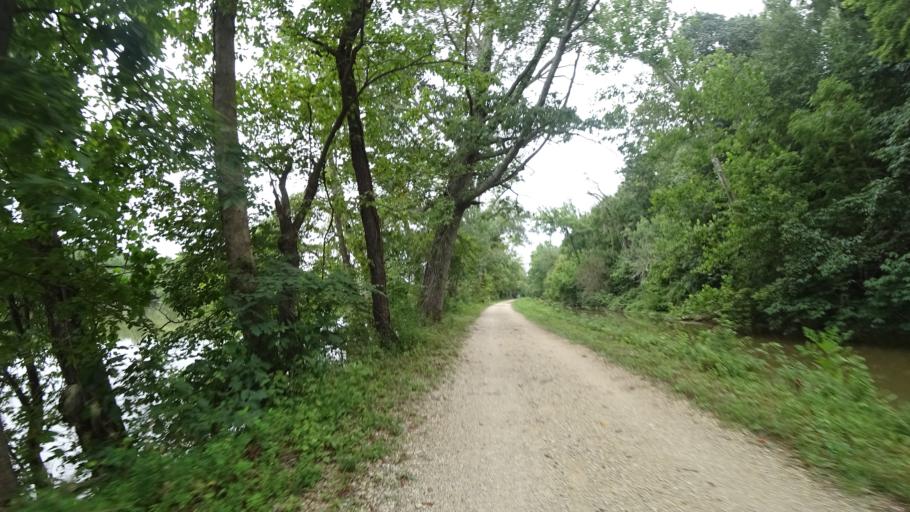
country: US
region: Maryland
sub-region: Montgomery County
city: Travilah
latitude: 39.0409
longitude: -77.2648
